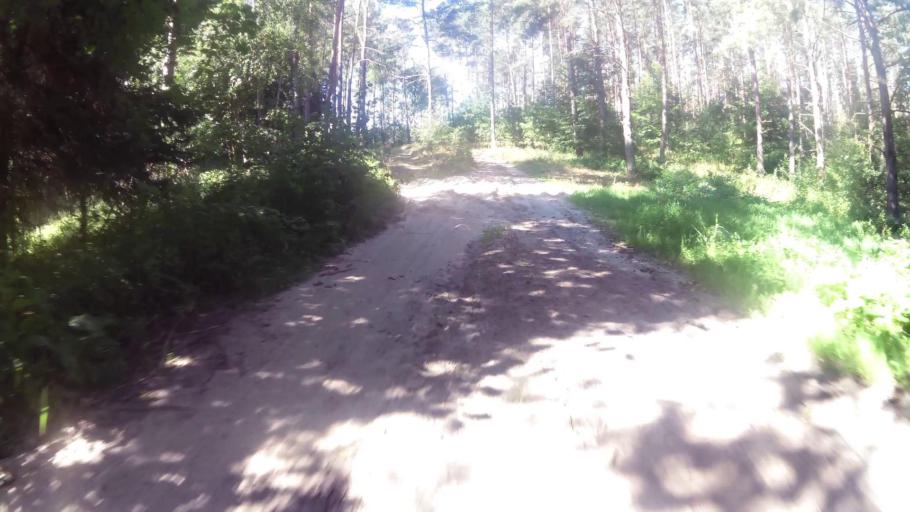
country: PL
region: West Pomeranian Voivodeship
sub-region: Powiat drawski
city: Drawsko Pomorskie
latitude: 53.5320
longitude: 15.7068
